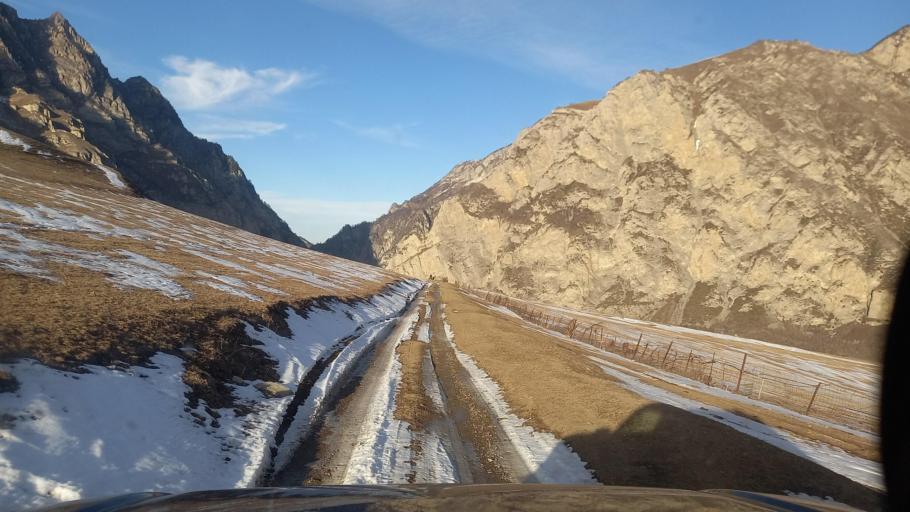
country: RU
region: Ingushetiya
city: Dzhayrakh
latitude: 42.8525
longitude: 44.5148
